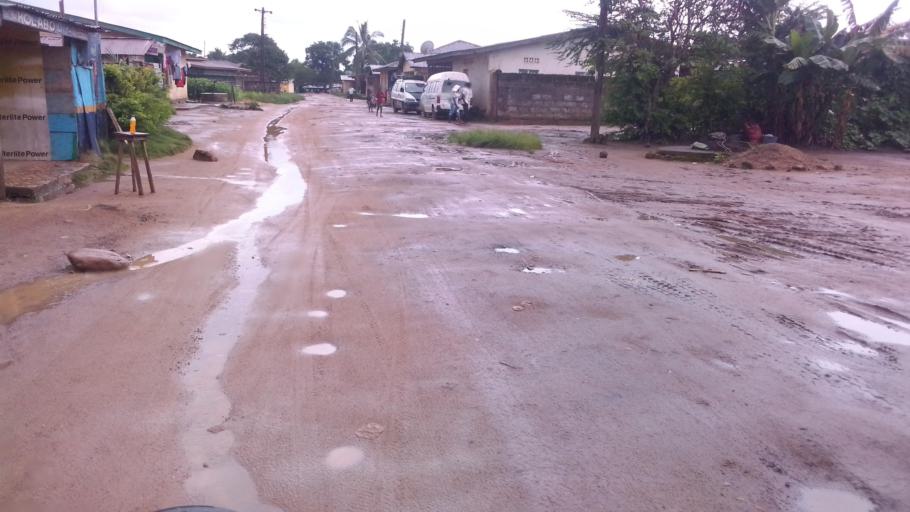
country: SL
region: Eastern Province
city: Kenema
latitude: 7.8844
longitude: -11.1795
